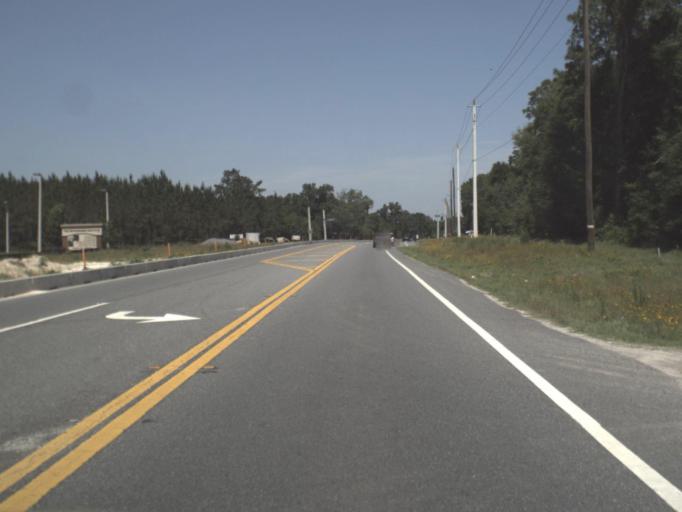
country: US
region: Florida
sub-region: Columbia County
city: Lake City
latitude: 30.1869
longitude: -82.7150
